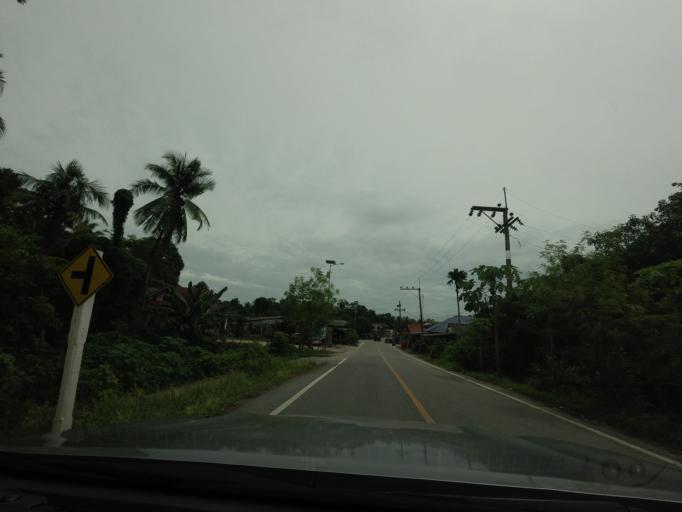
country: TH
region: Pattani
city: Kapho
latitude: 6.5926
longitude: 101.5310
